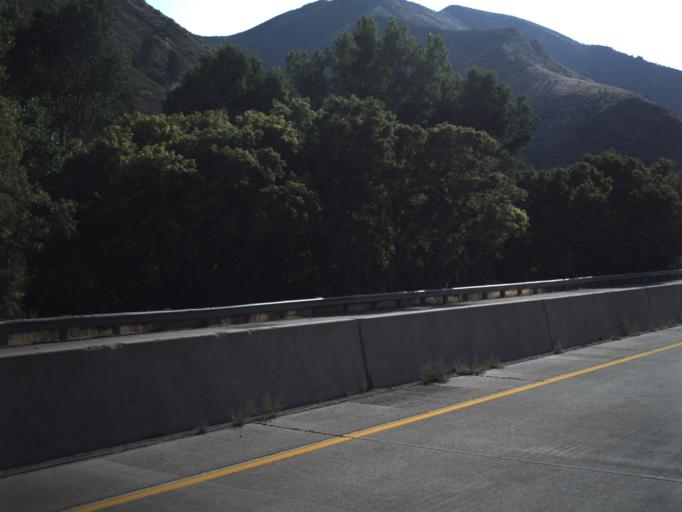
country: US
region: Utah
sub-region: Morgan County
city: Morgan
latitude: 41.0613
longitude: -111.5733
